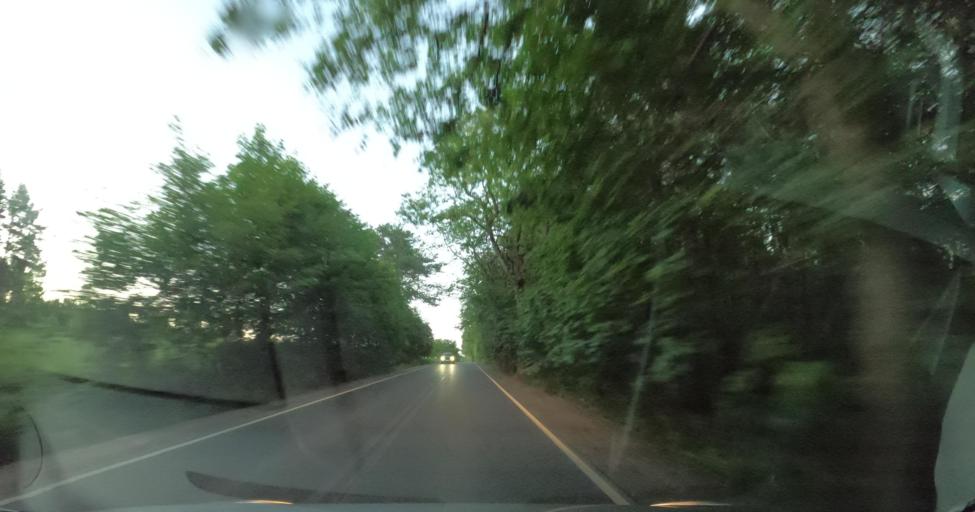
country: PL
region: Pomeranian Voivodeship
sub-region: Powiat wejherowski
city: Szemud
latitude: 54.4718
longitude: 18.1710
